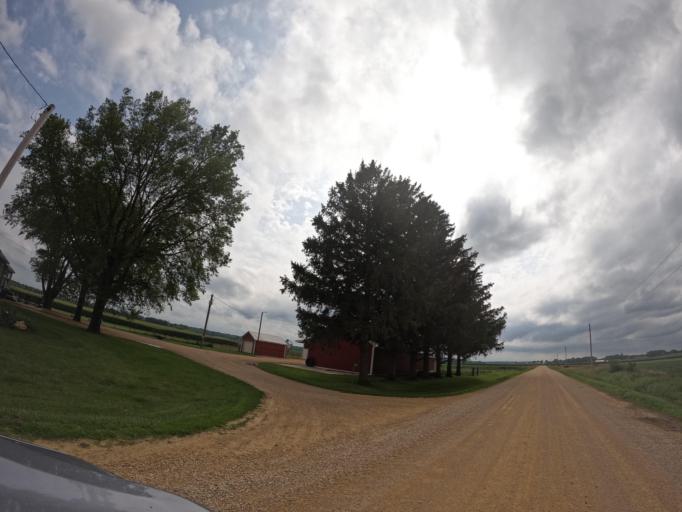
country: US
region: Iowa
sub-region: Clinton County
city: De Witt
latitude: 41.7858
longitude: -90.5770
